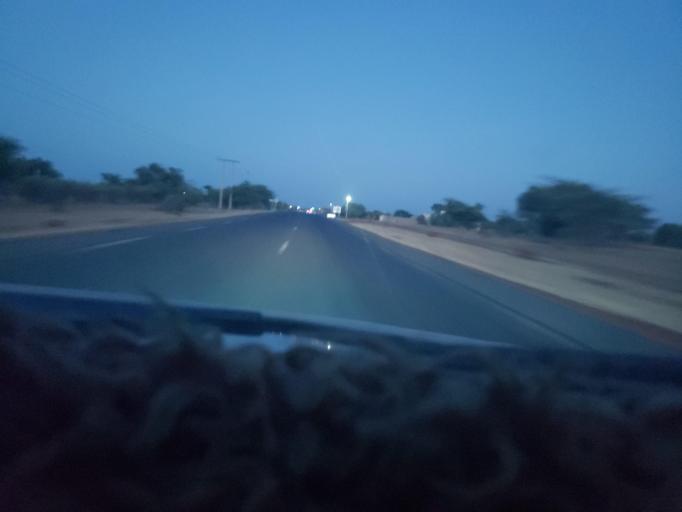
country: SN
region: Louga
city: Ndibene Dahra
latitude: 15.3809
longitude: -15.2458
